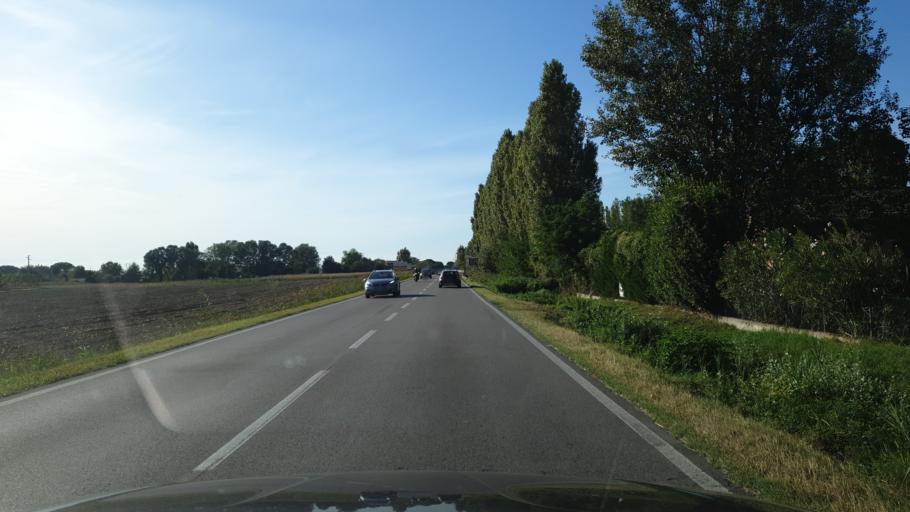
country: IT
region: Emilia-Romagna
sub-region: Provincia di Ravenna
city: Mezzano
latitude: 44.4517
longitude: 12.1153
